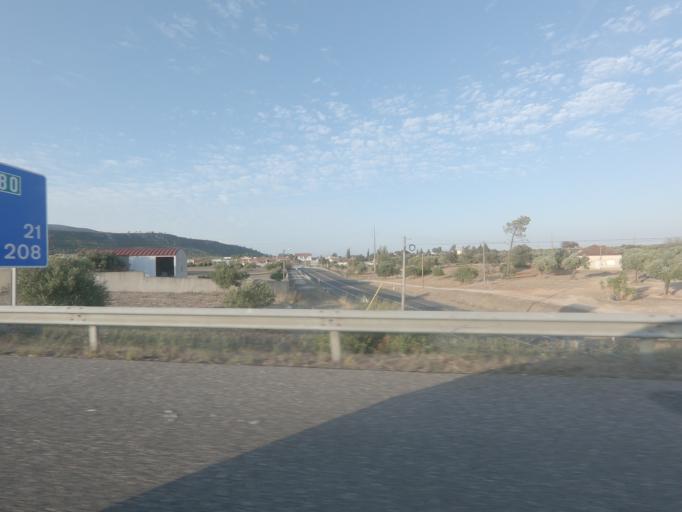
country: PT
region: Santarem
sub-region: Alcanena
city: Alcanena
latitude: 39.4807
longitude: -8.6345
